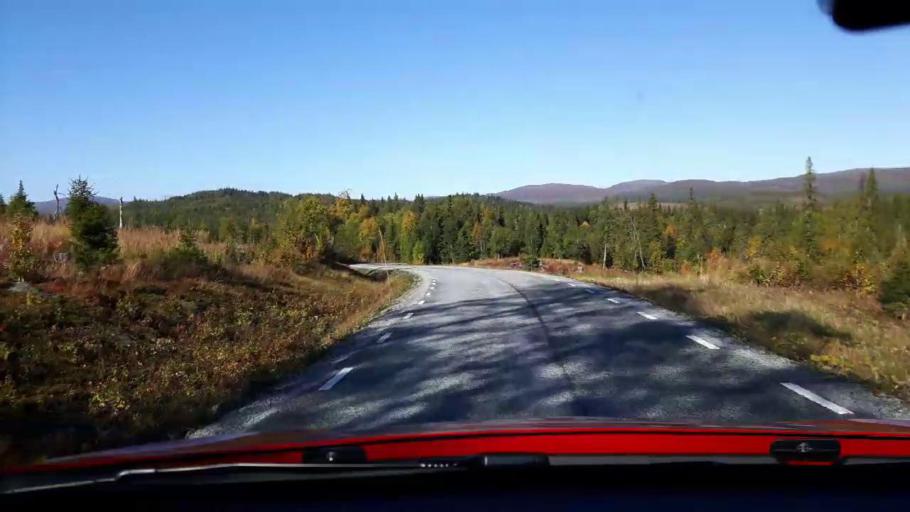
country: NO
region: Nord-Trondelag
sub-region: Lierne
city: Sandvika
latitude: 64.6227
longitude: 13.6955
